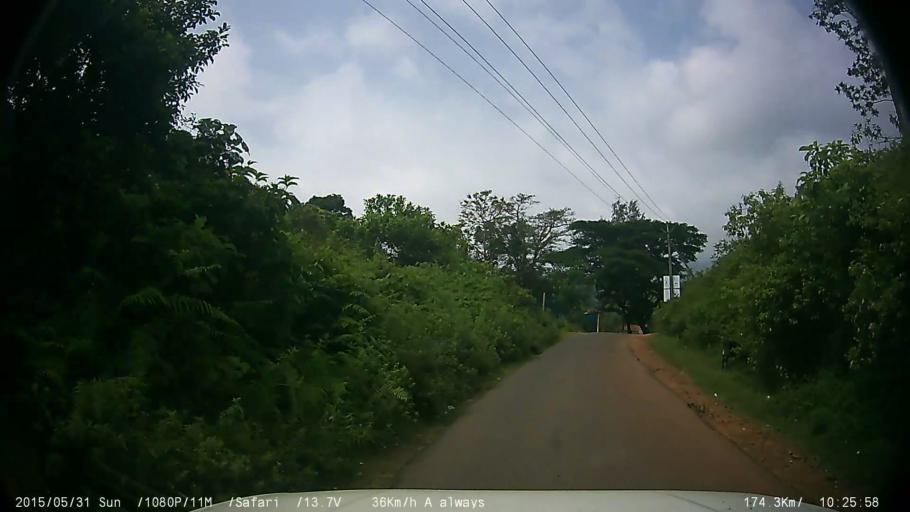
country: IN
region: Kerala
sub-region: Wayanad
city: Kalpetta
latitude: 11.5283
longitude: 76.1407
